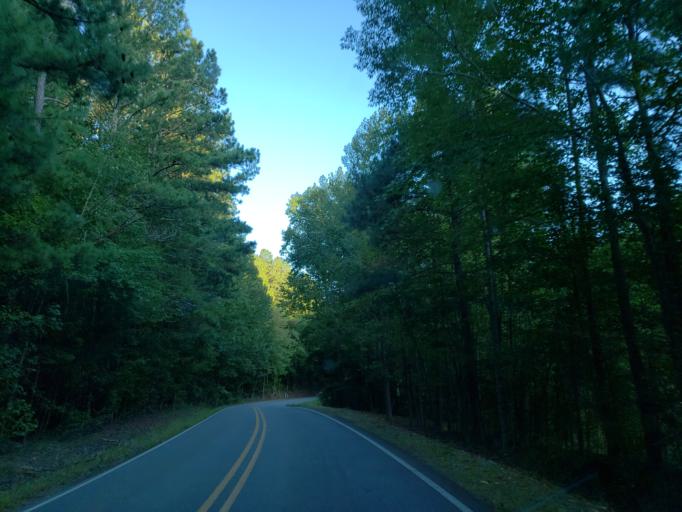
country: US
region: Georgia
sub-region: Bartow County
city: Rydal
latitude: 34.3878
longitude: -84.5931
